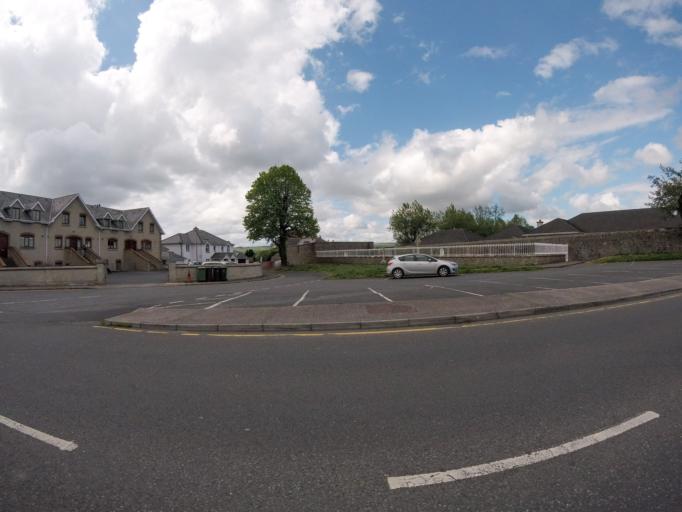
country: IE
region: Munster
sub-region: Waterford
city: Dungarvan
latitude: 52.0865
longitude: -7.6286
